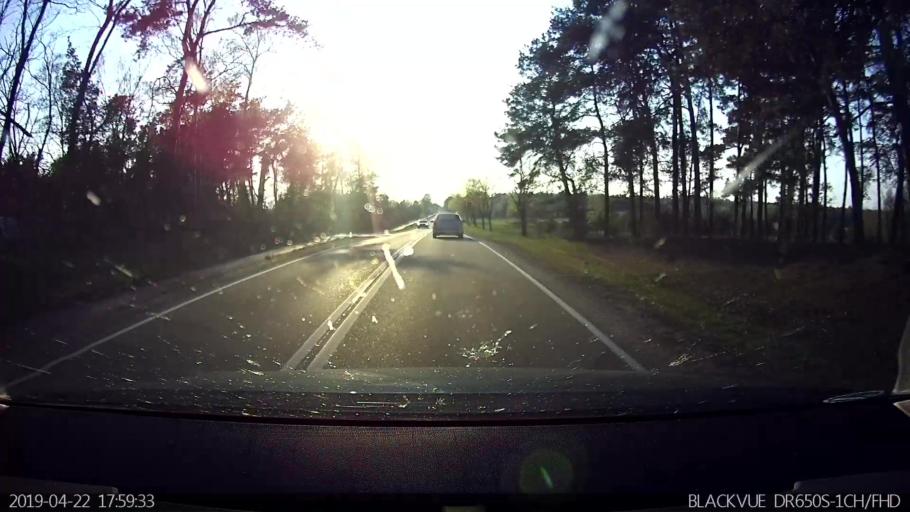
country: PL
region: Masovian Voivodeship
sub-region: Powiat wegrowski
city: Korytnica
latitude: 52.4740
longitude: 21.8610
